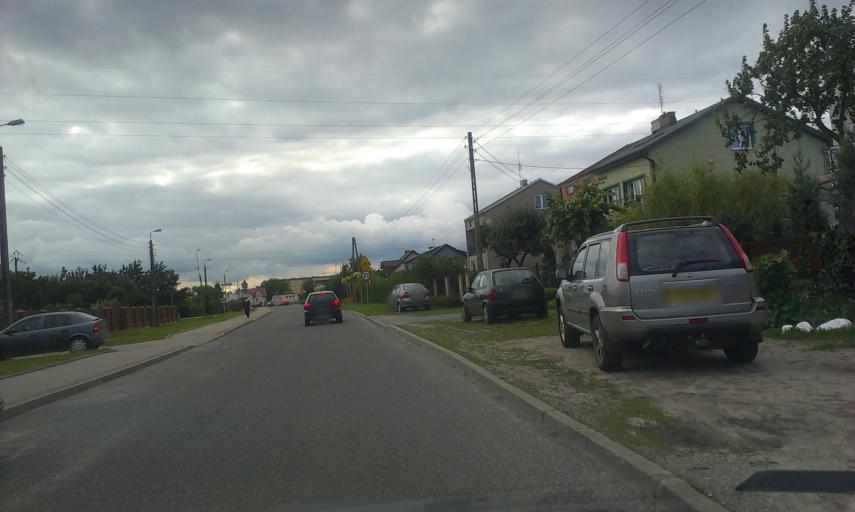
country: PL
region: Masovian Voivodeship
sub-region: Powiat zyrardowski
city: Mszczonow
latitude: 51.9753
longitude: 20.5333
